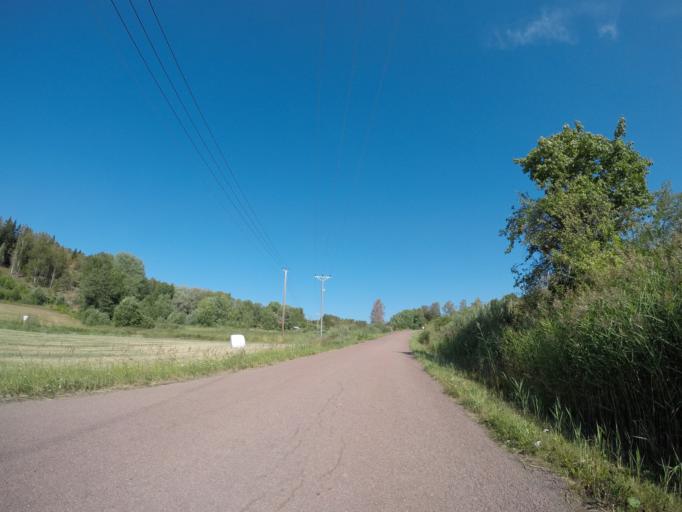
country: AX
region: Alands landsbygd
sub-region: Finstroem
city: Finstroem
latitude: 60.2714
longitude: 19.9237
